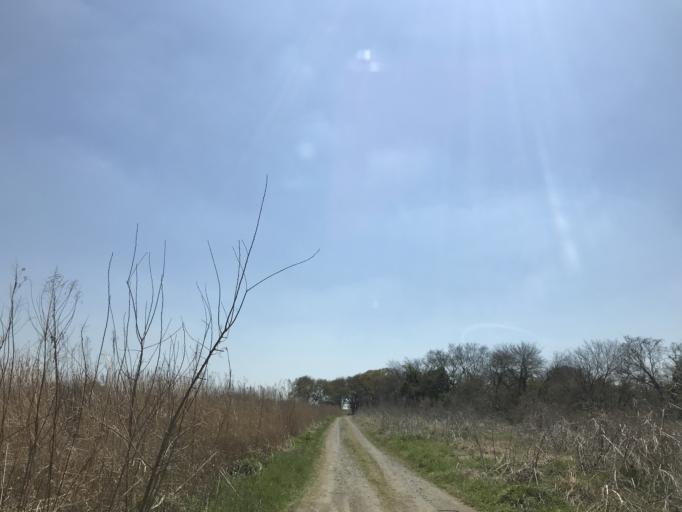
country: JP
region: Ibaraki
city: Moriya
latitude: 35.9325
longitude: 139.9742
